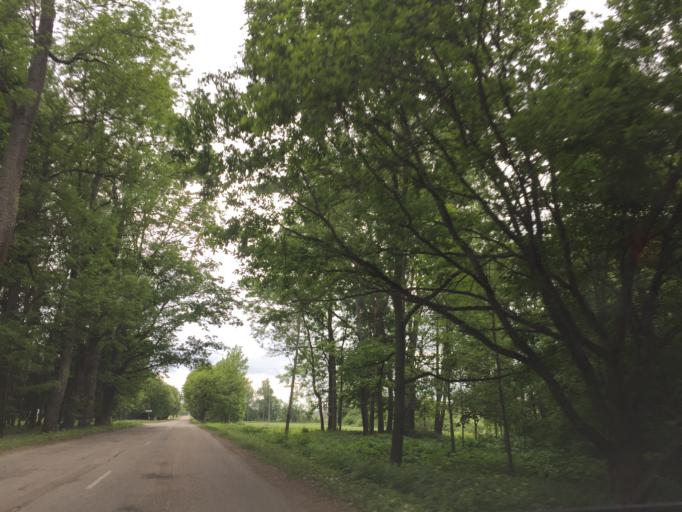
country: LV
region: Preilu Rajons
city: Preili
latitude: 56.0662
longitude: 26.7595
